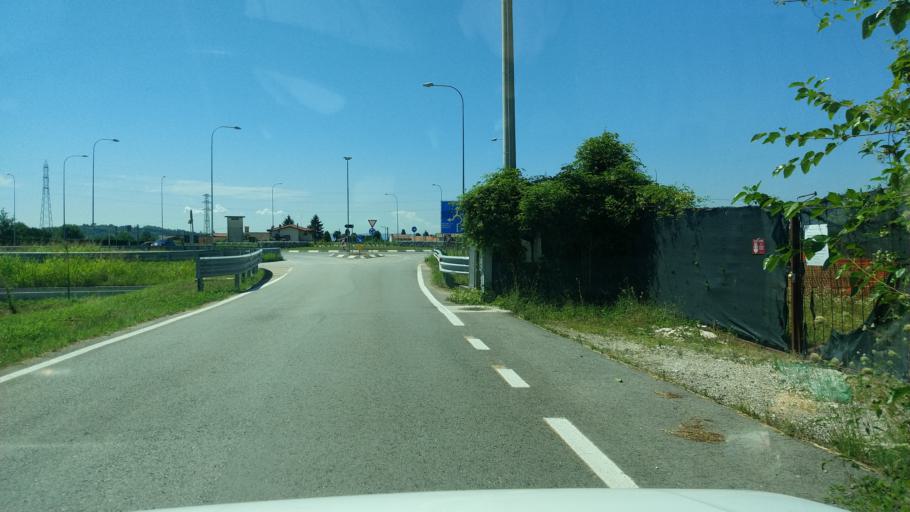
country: IT
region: Veneto
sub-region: Provincia di Vicenza
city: Sarcedo
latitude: 45.6942
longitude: 11.5392
